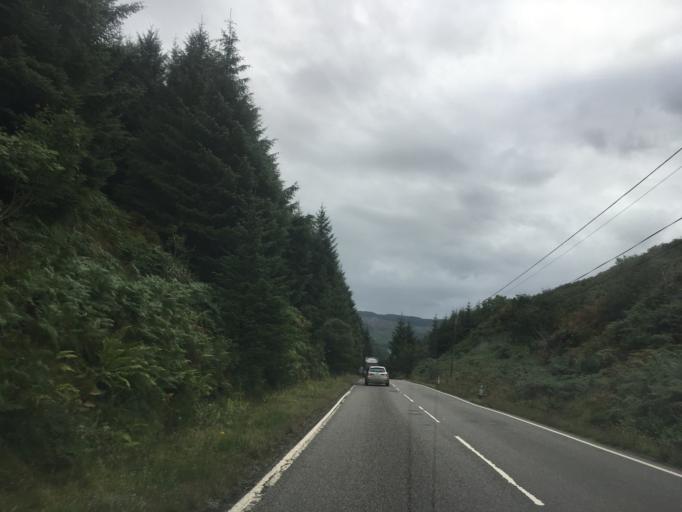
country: GB
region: Scotland
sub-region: Argyll and Bute
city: Oban
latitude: 56.2831
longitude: -5.4817
